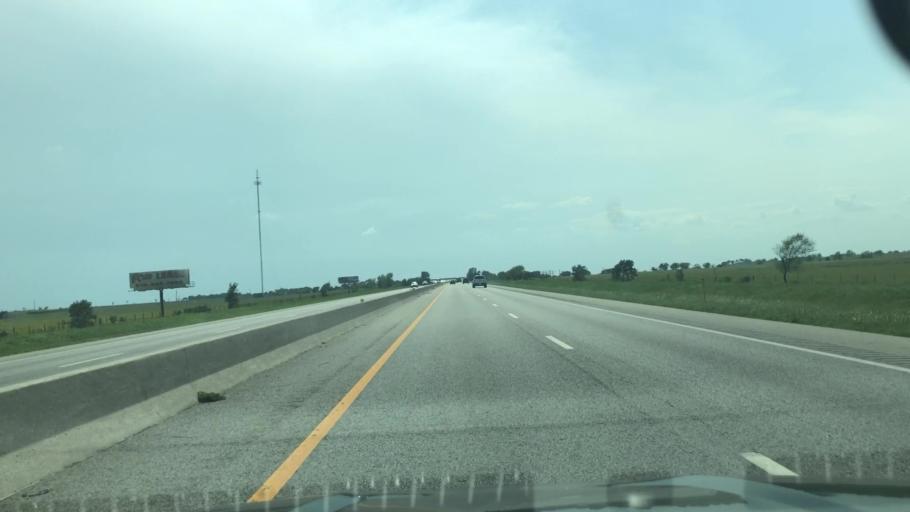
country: US
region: Oklahoma
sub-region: Ottawa County
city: Afton
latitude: 36.7039
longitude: -94.9861
